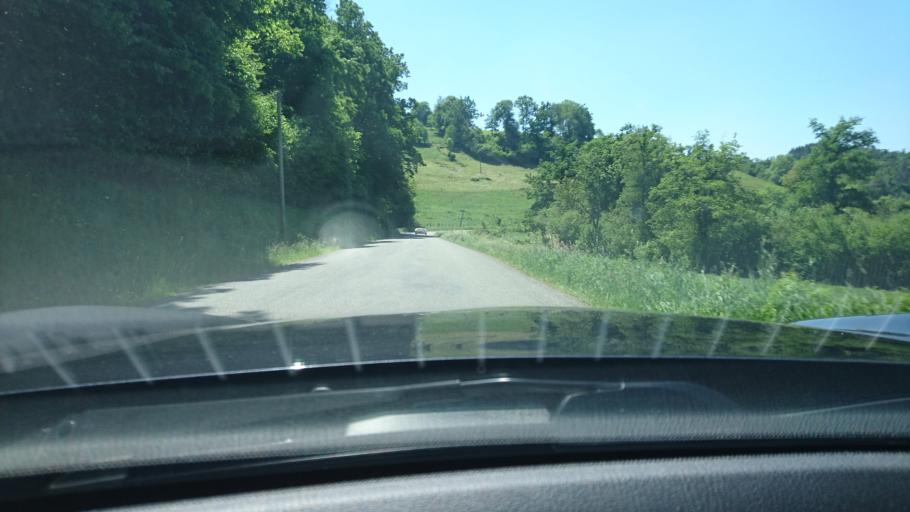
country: FR
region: Rhone-Alpes
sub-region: Departement de la Loire
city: Panissieres
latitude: 45.7845
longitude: 4.3196
